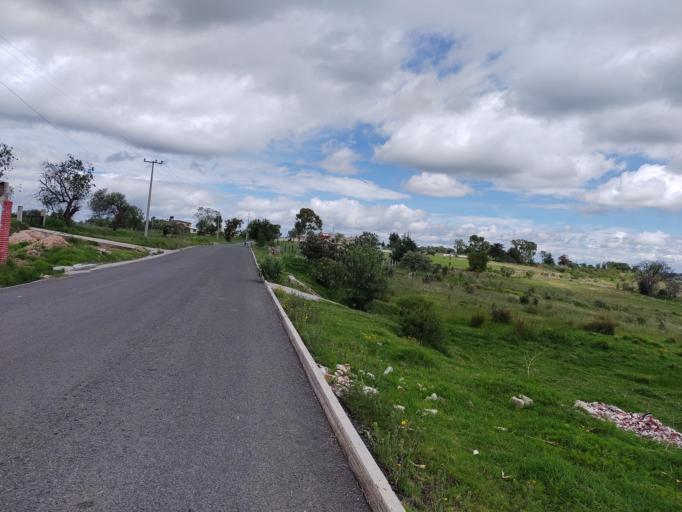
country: MX
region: Mexico
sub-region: Aculco
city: Gunyo Poniente (San Jose Gunyo)
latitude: 20.1162
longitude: -99.8755
